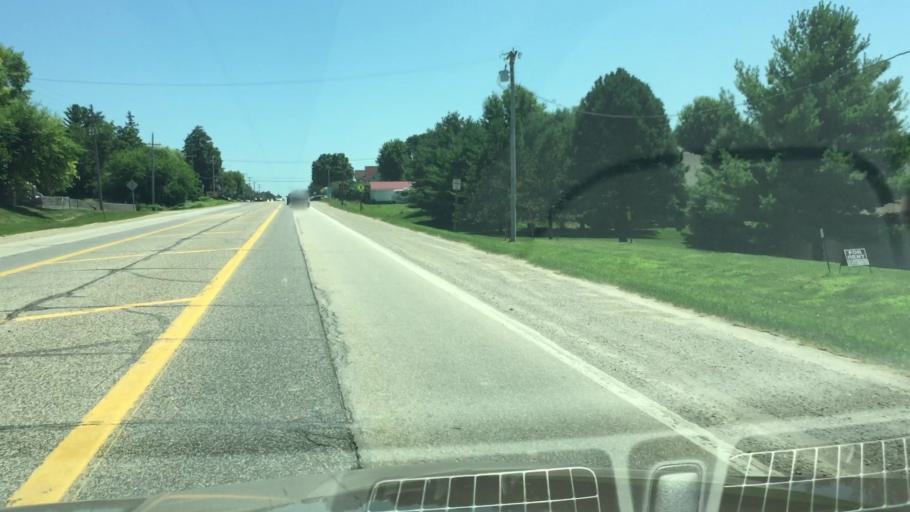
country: US
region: Iowa
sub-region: Linn County
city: Lisbon
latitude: 41.9178
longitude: -91.3886
